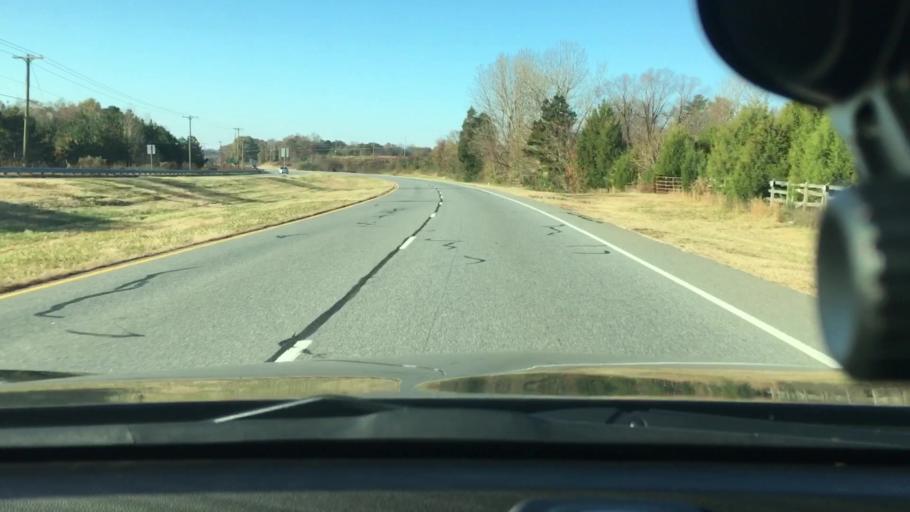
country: US
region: North Carolina
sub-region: Cabarrus County
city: Concord
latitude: 35.3845
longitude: -80.5235
